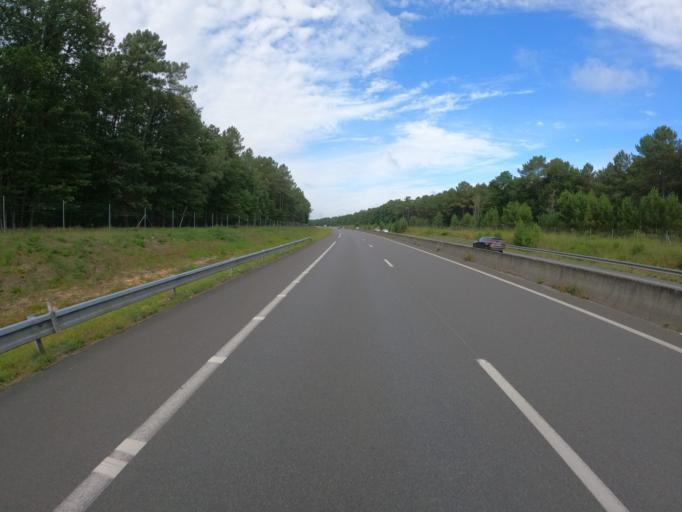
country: FR
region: Centre
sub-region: Departement d'Indre-et-Loire
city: Langeais
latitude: 47.3458
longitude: 0.3648
